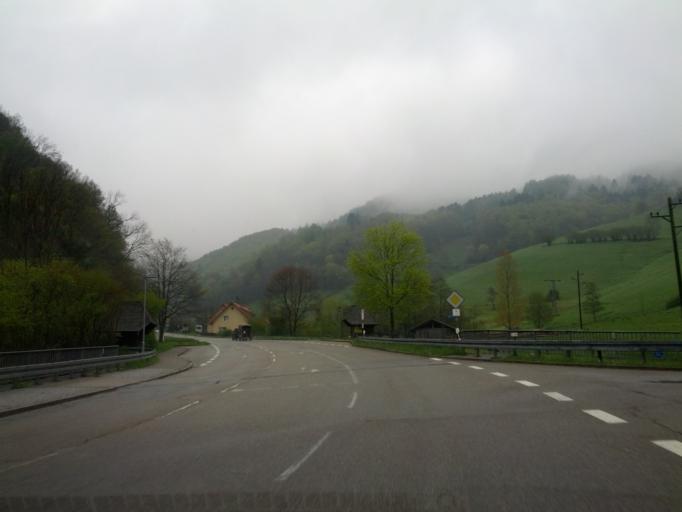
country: DE
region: Baden-Wuerttemberg
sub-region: Freiburg Region
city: Wieden
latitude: 47.8767
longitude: 7.8383
